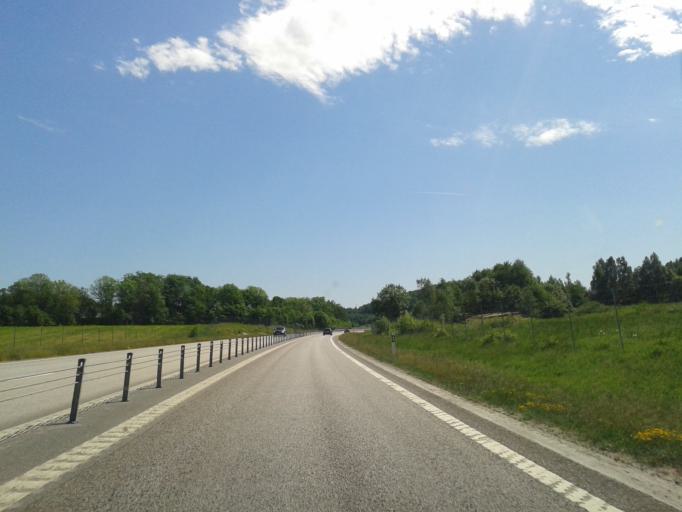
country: SE
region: Vaestra Goetaland
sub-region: Orust
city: Henan
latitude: 58.3503
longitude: 11.7425
